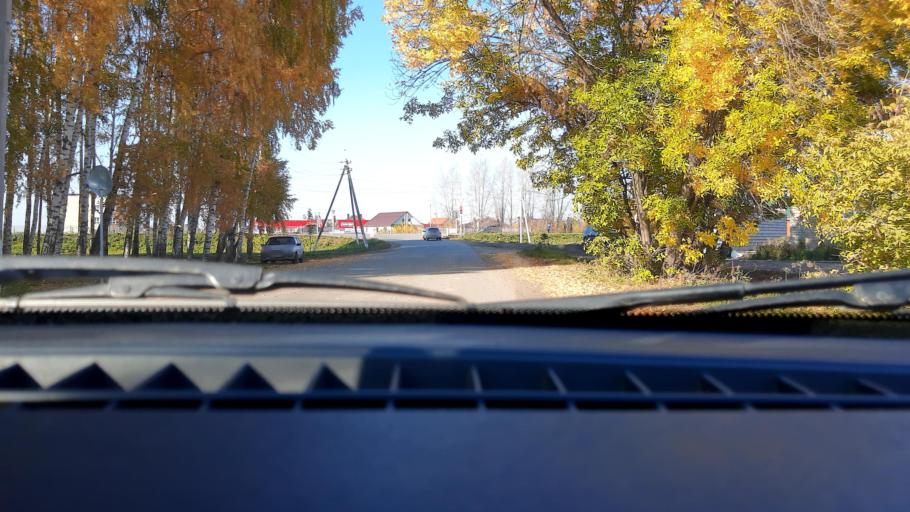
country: RU
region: Bashkortostan
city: Mikhaylovka
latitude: 54.7825
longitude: 55.8362
